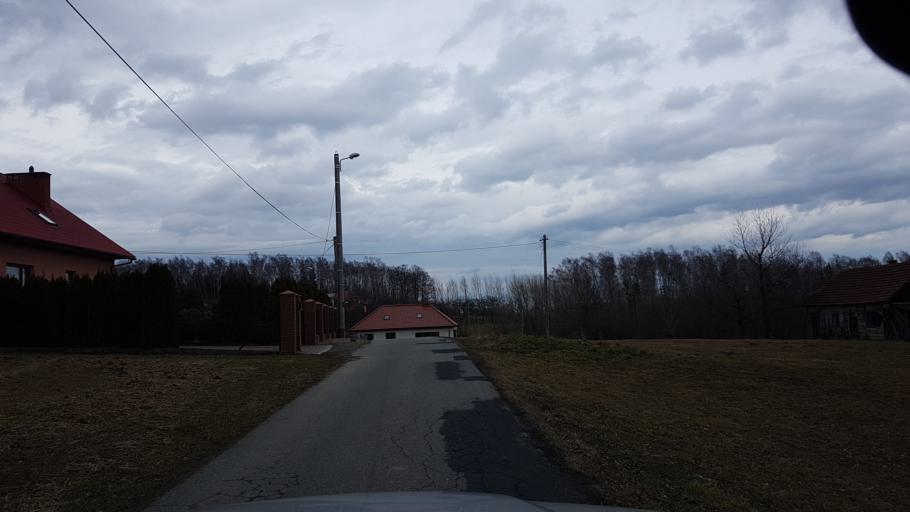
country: PL
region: Lesser Poland Voivodeship
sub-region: Powiat nowosadecki
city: Stary Sacz
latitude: 49.5274
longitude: 20.6227
